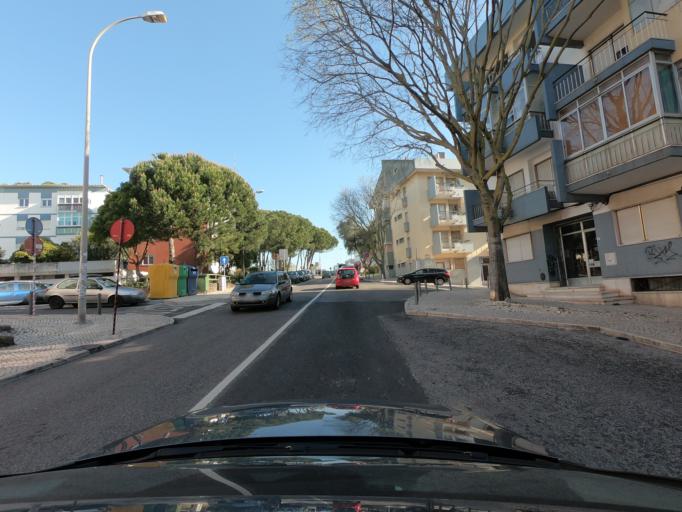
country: PT
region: Lisbon
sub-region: Oeiras
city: Oeiras
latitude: 38.6972
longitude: -9.3062
